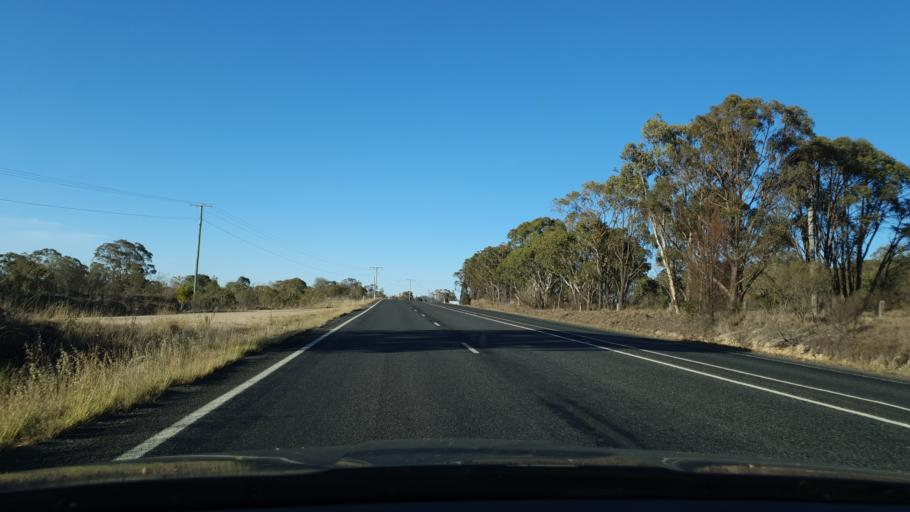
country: AU
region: Queensland
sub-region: Southern Downs
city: Stanthorpe
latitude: -28.6944
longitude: 151.9070
